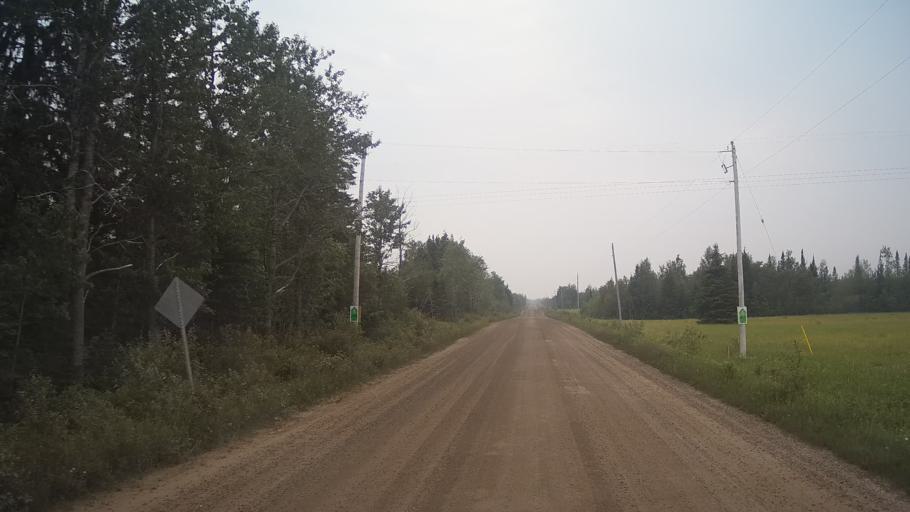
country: CA
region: Ontario
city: Hearst
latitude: 49.6423
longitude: -83.2783
